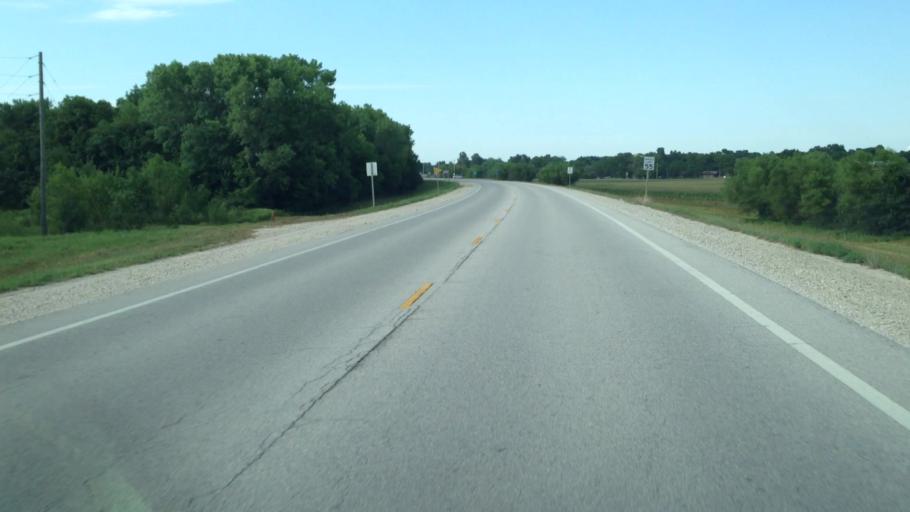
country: US
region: Kansas
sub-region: Neosho County
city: Erie
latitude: 37.5611
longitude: -95.2542
